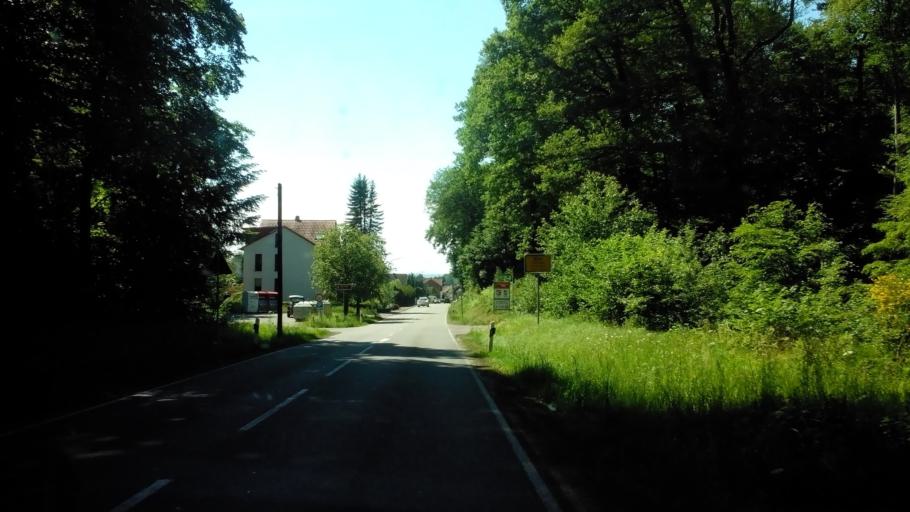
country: DE
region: Saarland
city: Puttlingen
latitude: 49.3055
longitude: 6.8650
